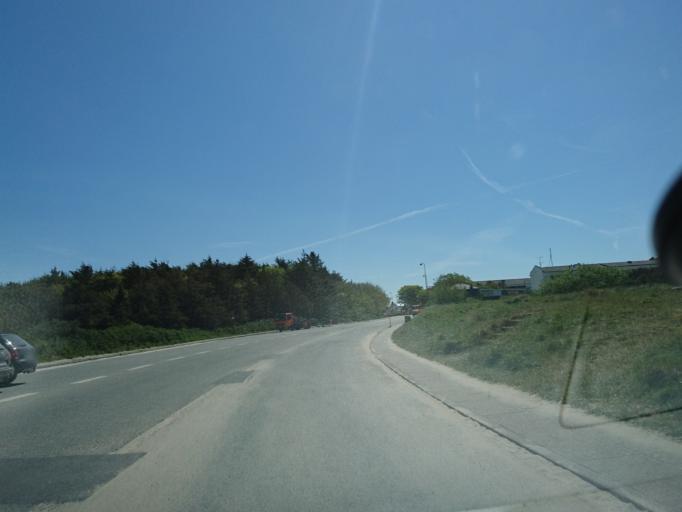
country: DK
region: North Denmark
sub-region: Hjorring Kommune
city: Sindal
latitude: 57.5947
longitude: 10.1843
